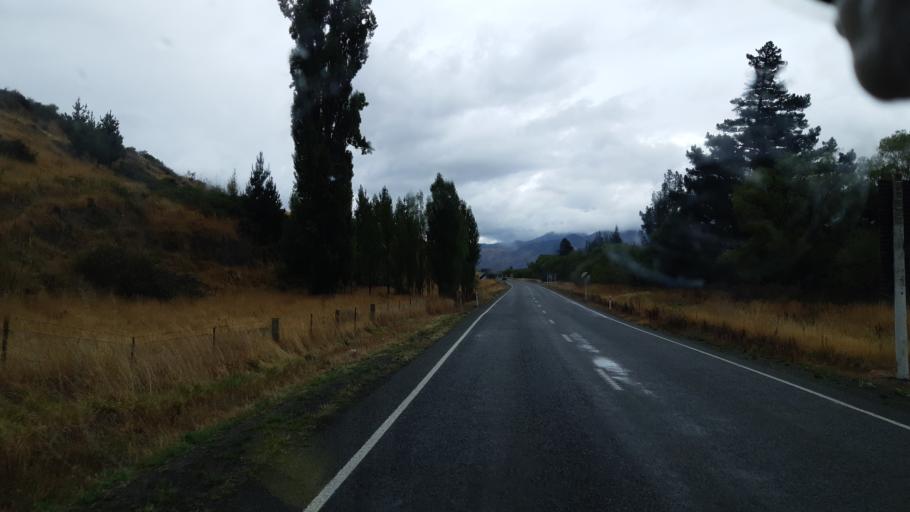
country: NZ
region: Canterbury
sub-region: Hurunui District
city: Amberley
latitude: -42.5804
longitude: 172.7708
